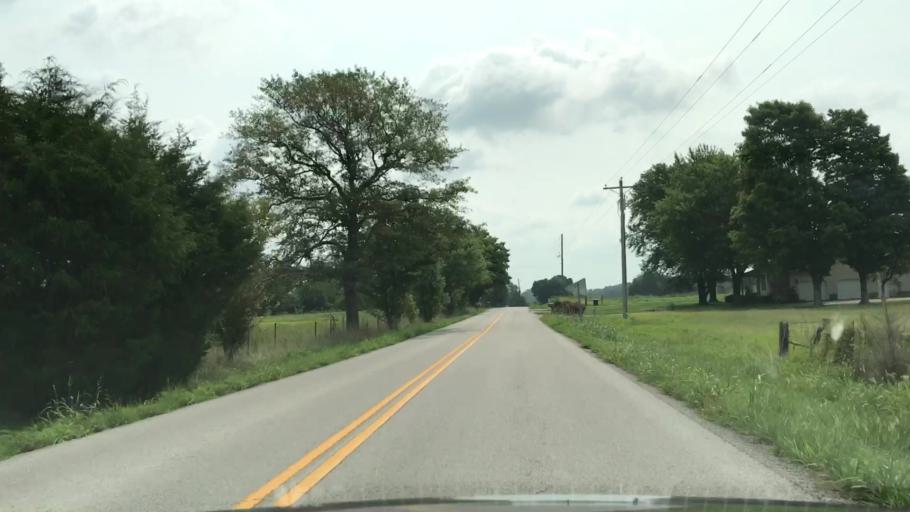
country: US
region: Kentucky
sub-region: Edmonson County
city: Brownsville
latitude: 37.1322
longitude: -86.1689
